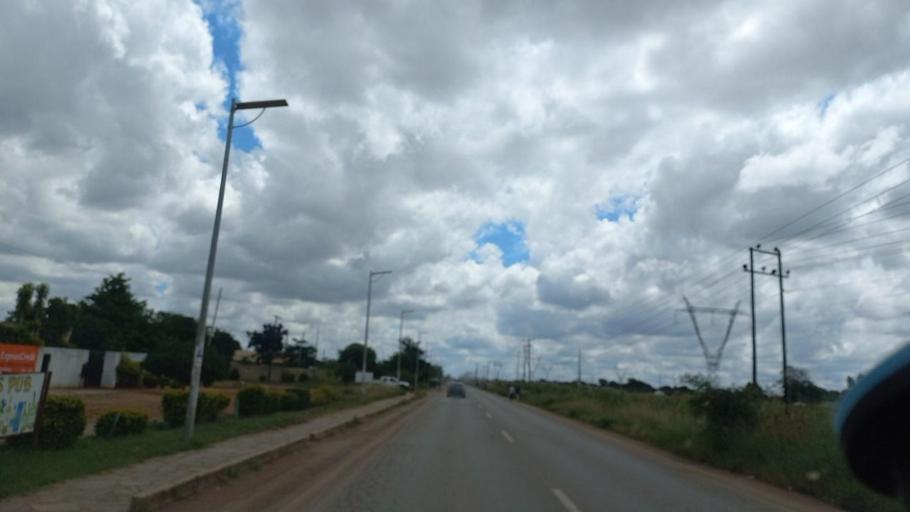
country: ZM
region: Lusaka
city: Lusaka
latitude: -15.4584
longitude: 28.3326
